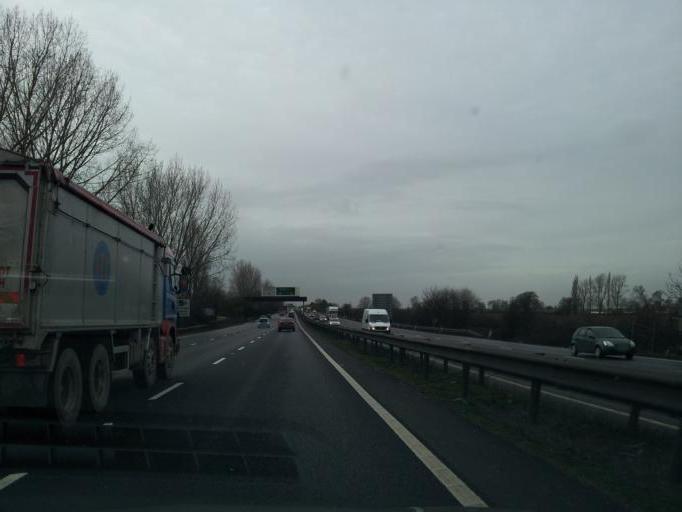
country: GB
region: England
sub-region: Cambridgeshire
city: Girton
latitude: 52.2495
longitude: 0.0402
